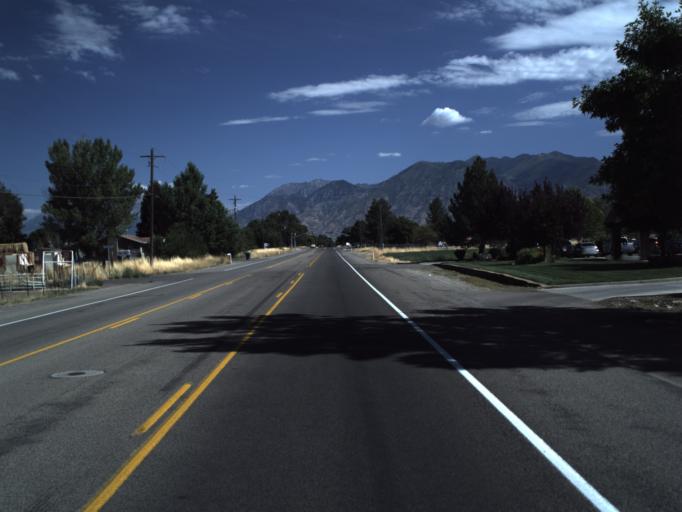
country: US
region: Utah
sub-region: Utah County
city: Salem
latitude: 40.0761
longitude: -111.6604
